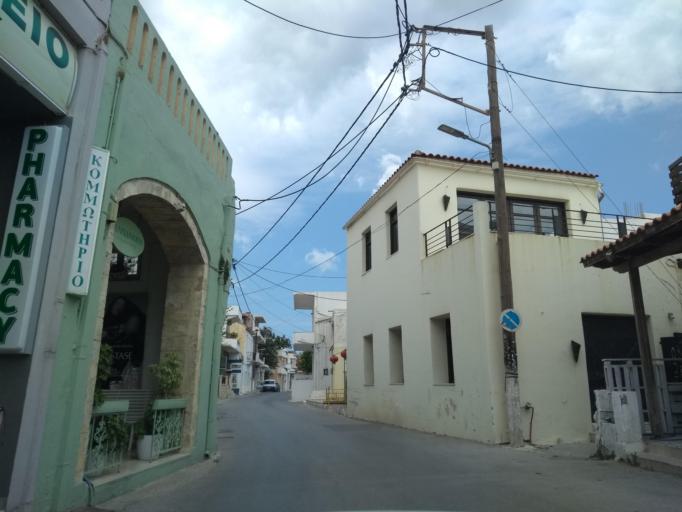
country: GR
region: Crete
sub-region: Nomos Chanias
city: Kalivai
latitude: 35.4536
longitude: 24.1721
